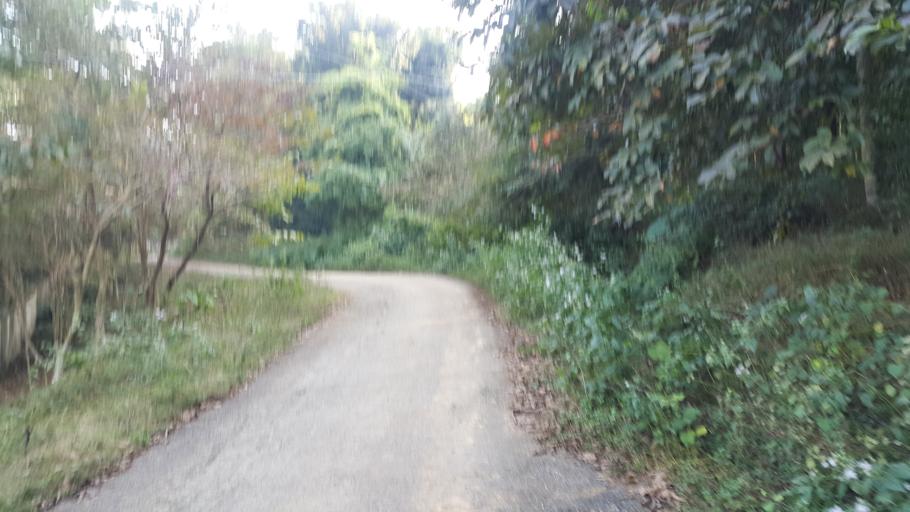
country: VN
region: Hoa Binh
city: Luong Son
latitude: 20.9164
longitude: 105.5750
